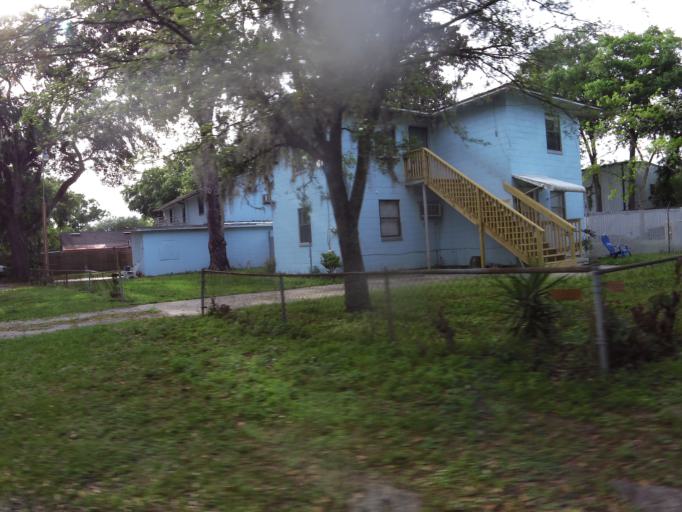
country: US
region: Florida
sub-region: Duval County
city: Jacksonville
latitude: 30.3326
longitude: -81.6010
